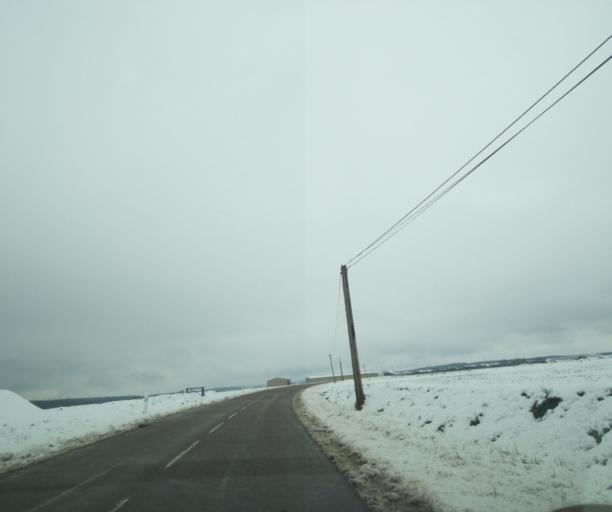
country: FR
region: Champagne-Ardenne
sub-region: Departement de la Haute-Marne
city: Montier-en-Der
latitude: 48.4473
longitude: 4.7997
